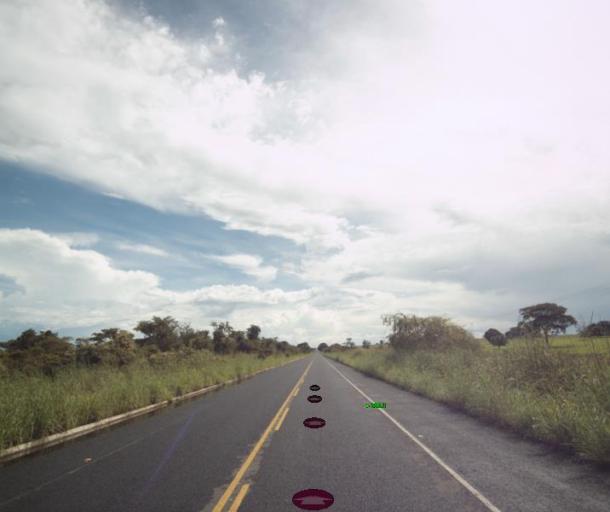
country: BR
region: Goias
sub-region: Sao Miguel Do Araguaia
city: Sao Miguel do Araguaia
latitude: -13.2944
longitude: -50.2299
